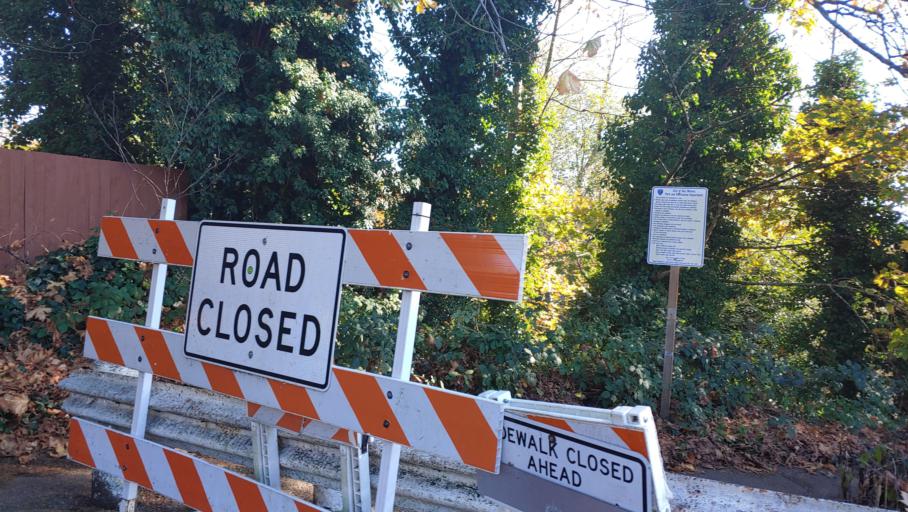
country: US
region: Washington
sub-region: King County
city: Des Moines
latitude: 47.4053
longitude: -122.3295
